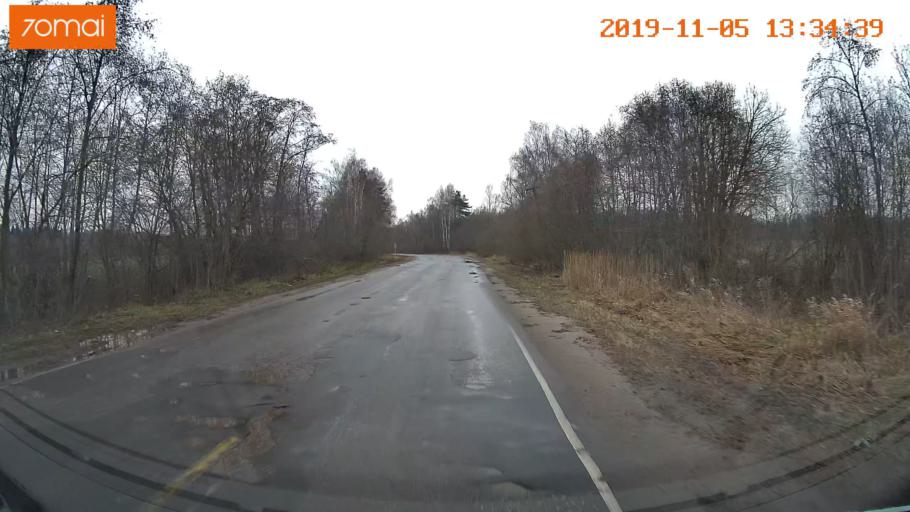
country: RU
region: Ivanovo
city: Shuya
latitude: 56.9023
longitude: 41.3899
